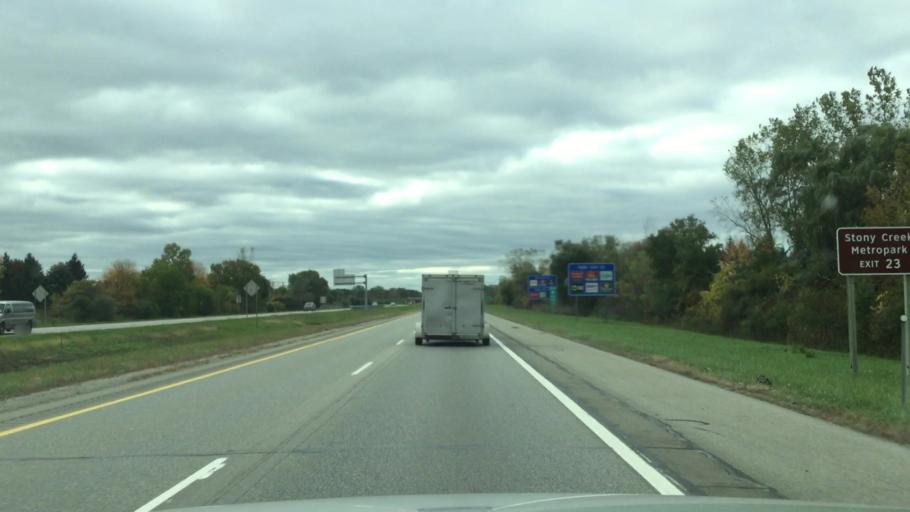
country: US
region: Michigan
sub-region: Macomb County
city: Shelby
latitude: 42.7242
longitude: -83.0266
